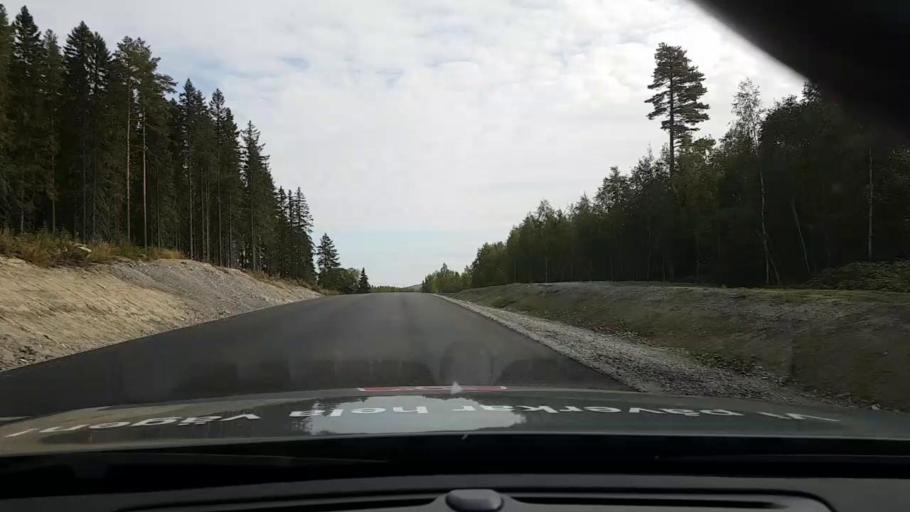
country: SE
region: Vaesternorrland
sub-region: OErnskoeldsviks Kommun
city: Bjasta
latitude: 63.2919
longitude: 18.5046
